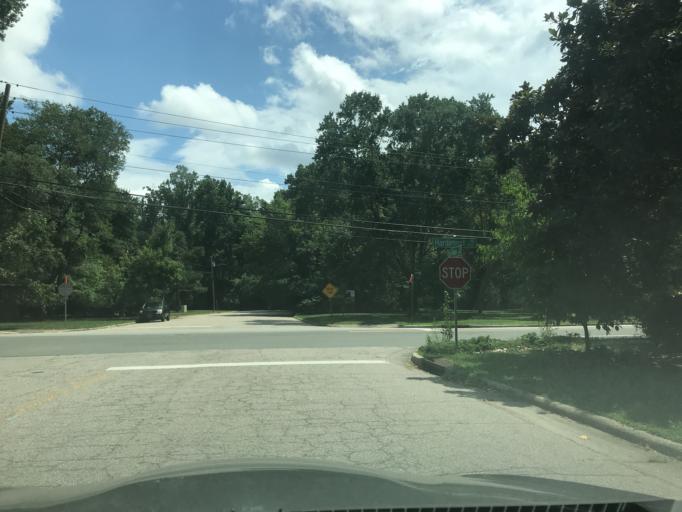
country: US
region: North Carolina
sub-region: Wake County
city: West Raleigh
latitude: 35.8363
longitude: -78.6254
